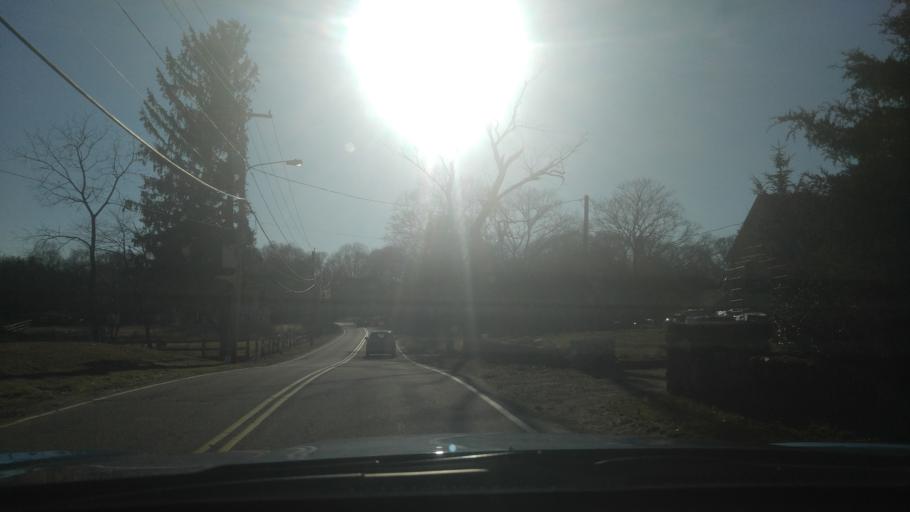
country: US
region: Rhode Island
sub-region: Washington County
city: North Kingstown
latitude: 41.5745
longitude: -71.4873
